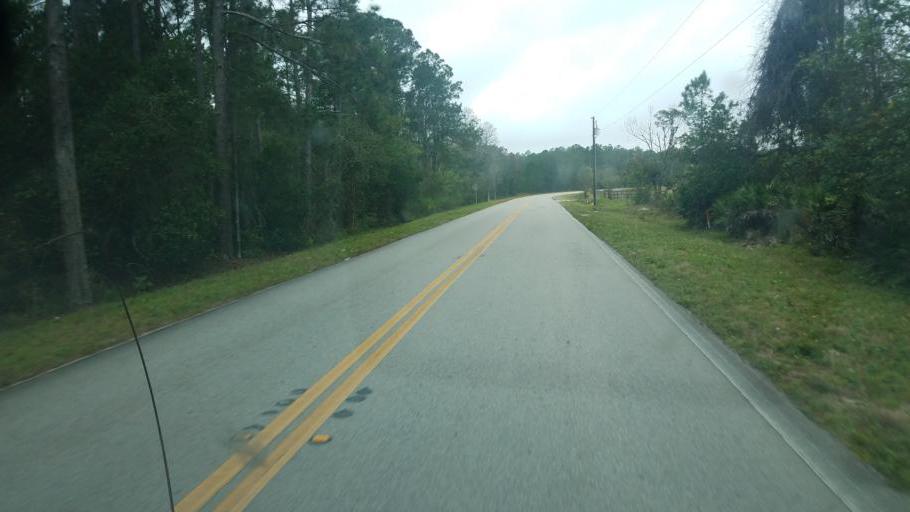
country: US
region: Florida
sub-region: Lake County
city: Four Corners
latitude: 28.2580
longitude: -81.7343
